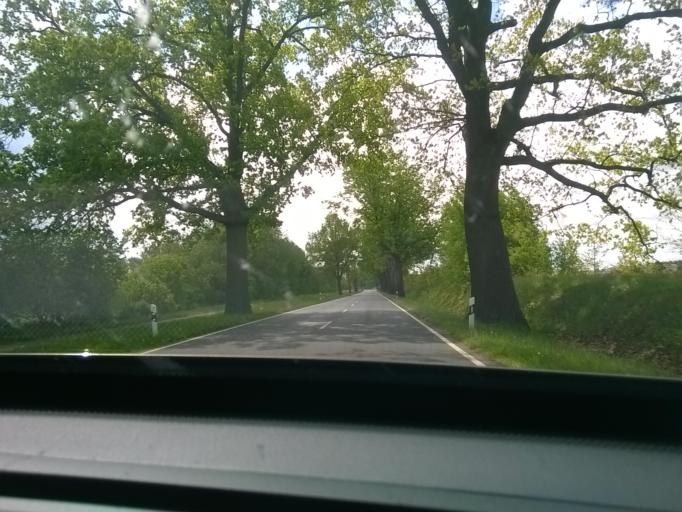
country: DE
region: Brandenburg
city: Wittstock
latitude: 53.1393
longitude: 12.4890
